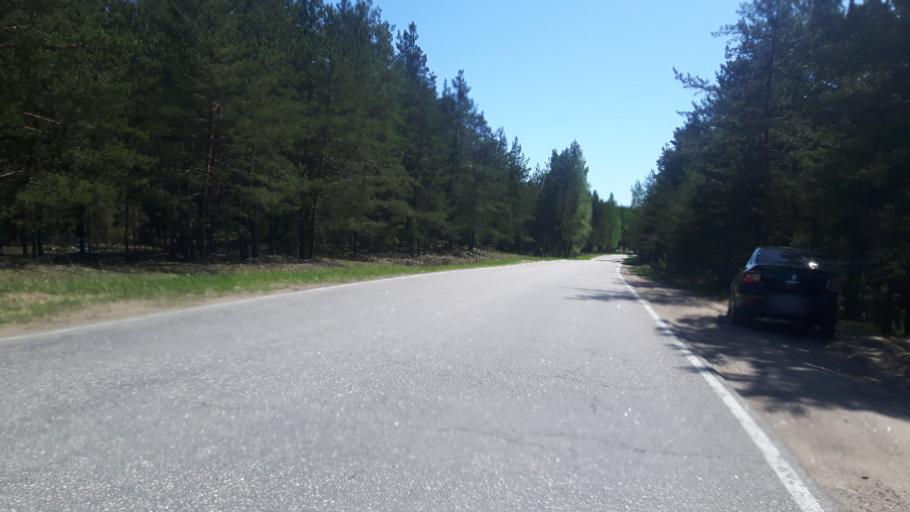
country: RU
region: Leningrad
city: Glebychevo
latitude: 60.3320
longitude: 28.8215
